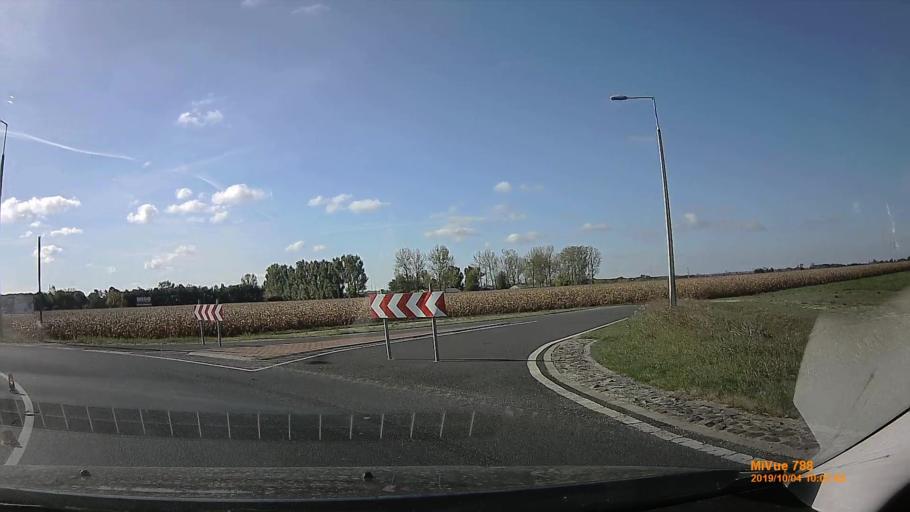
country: HU
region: Somogy
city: Kaposvar
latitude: 46.3957
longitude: 17.7777
